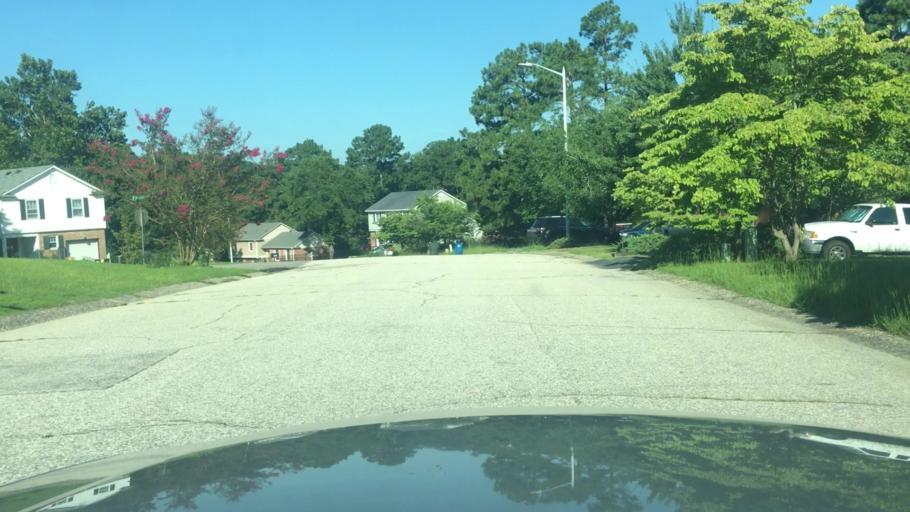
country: US
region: North Carolina
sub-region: Cumberland County
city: Spring Lake
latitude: 35.1384
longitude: -78.8928
